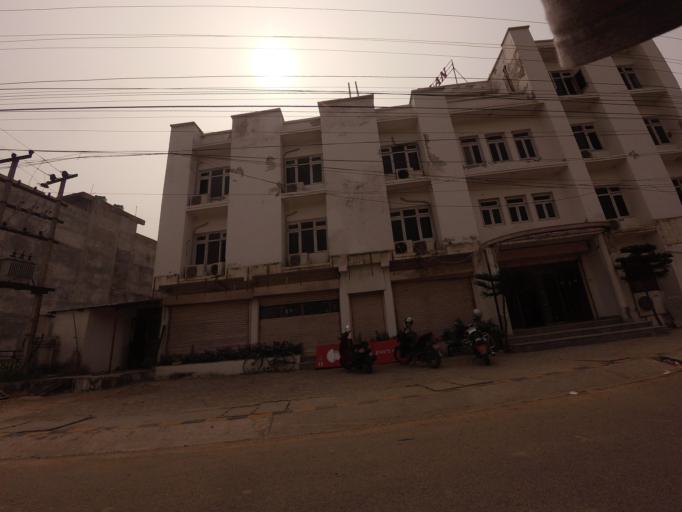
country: IN
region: Uttar Pradesh
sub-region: Maharajganj
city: Nautanwa
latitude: 27.4722
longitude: 83.2840
